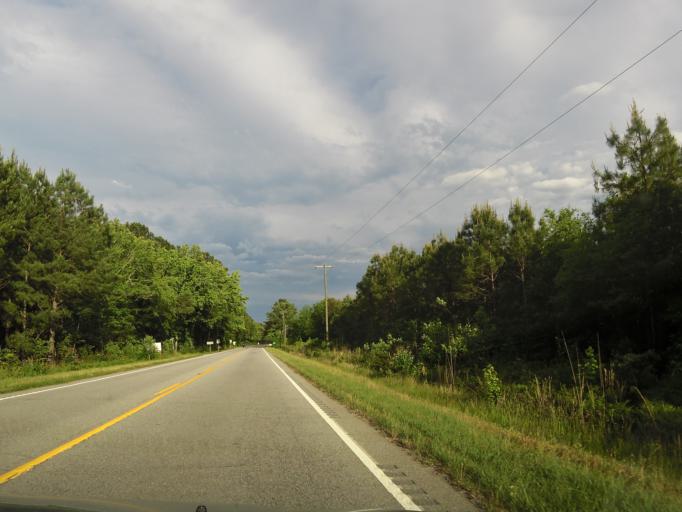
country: US
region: South Carolina
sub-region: Hampton County
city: Estill
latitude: 32.6006
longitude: -81.2280
